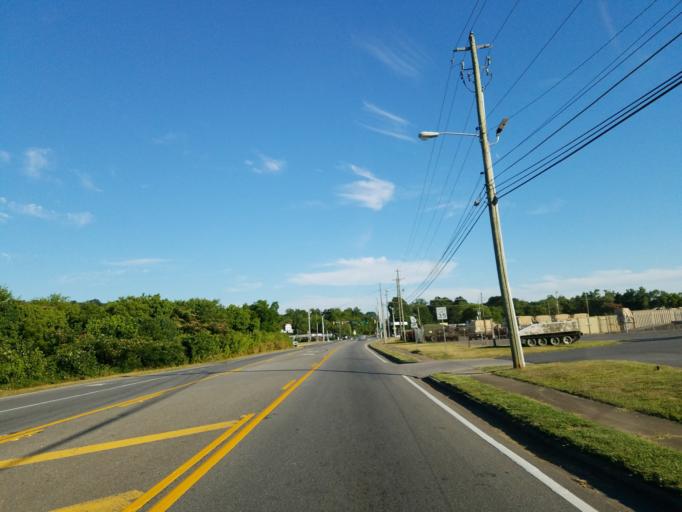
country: US
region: Georgia
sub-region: Gordon County
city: Calhoun
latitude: 34.5075
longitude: -84.9566
